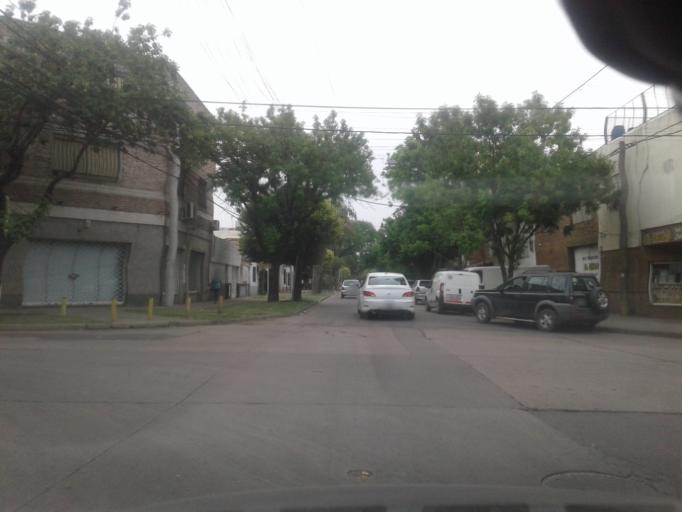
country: AR
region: Santa Fe
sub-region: Departamento de Rosario
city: Rosario
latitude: -32.9591
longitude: -60.6783
